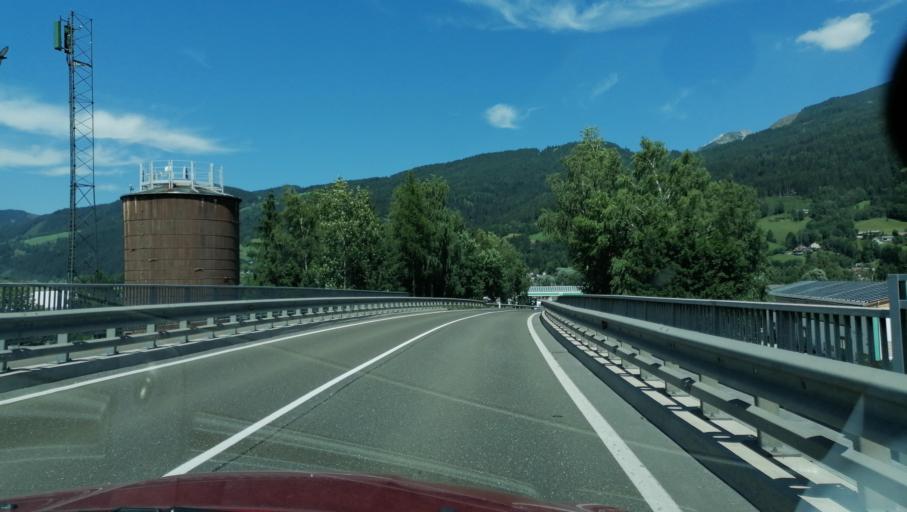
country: AT
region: Styria
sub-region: Politischer Bezirk Liezen
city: Trieben
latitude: 47.4916
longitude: 14.4833
